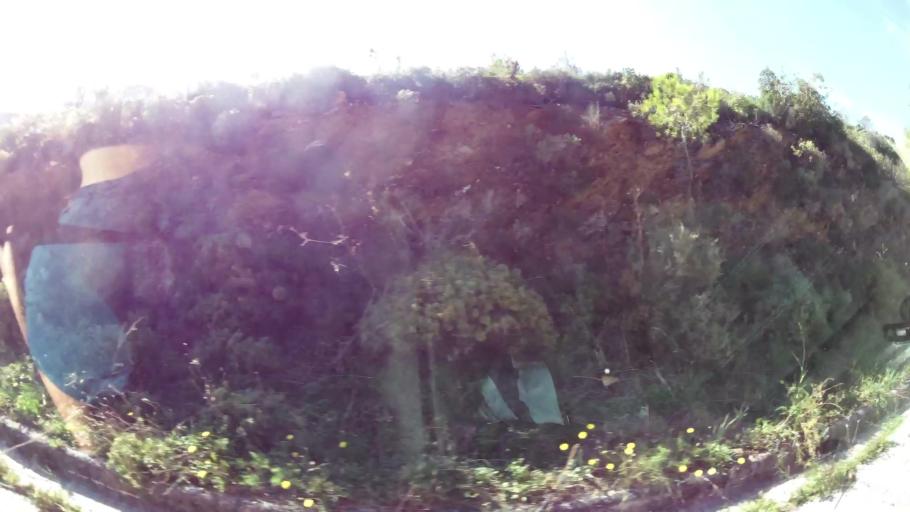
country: GR
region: Attica
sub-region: Nomarchia Anatolikis Attikis
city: Dhrafi
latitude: 38.0394
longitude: 23.9019
